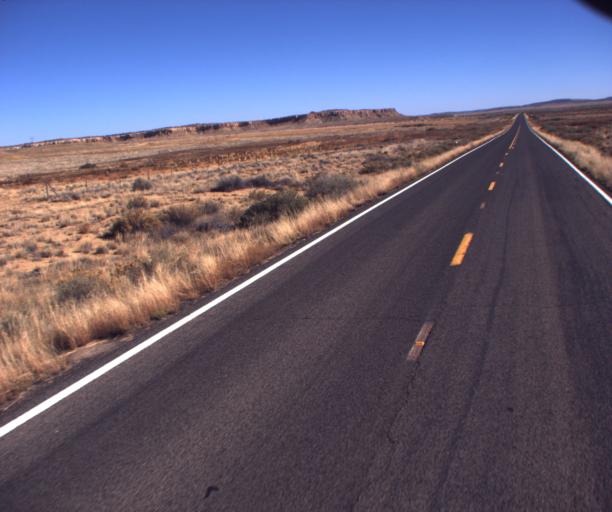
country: US
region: Arizona
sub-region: Navajo County
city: First Mesa
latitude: 35.9787
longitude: -110.7433
